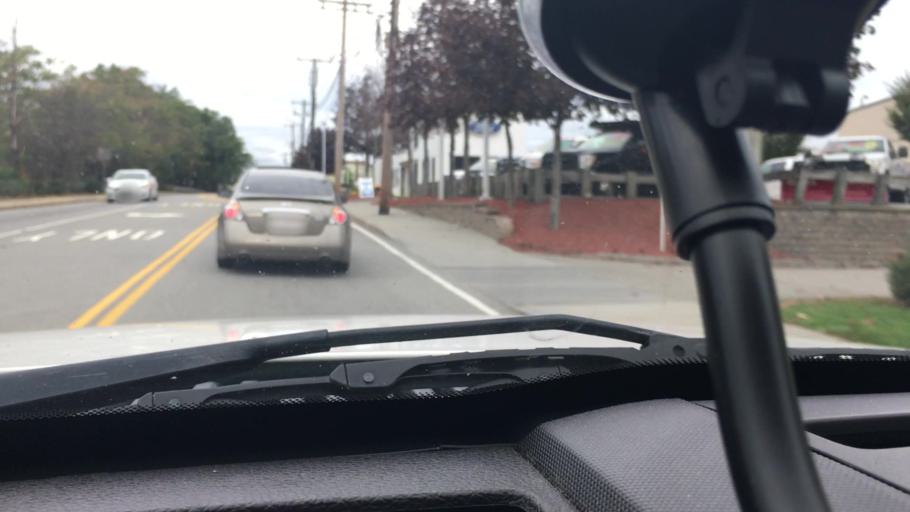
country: US
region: Massachusetts
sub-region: Middlesex County
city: Waltham
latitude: 42.3675
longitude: -71.2138
